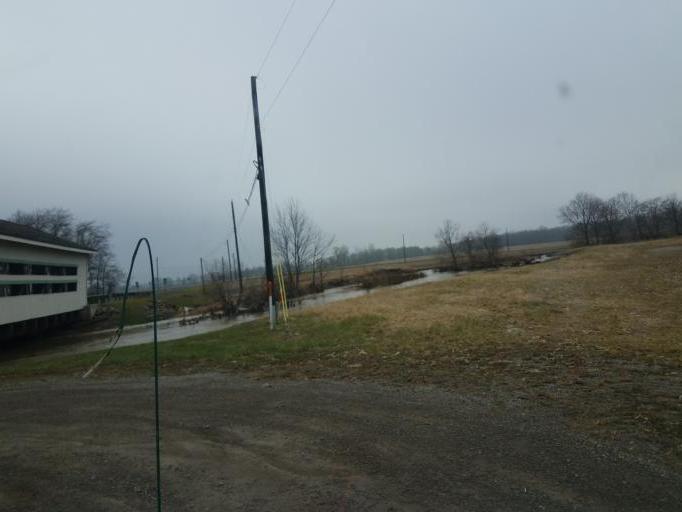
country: US
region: Ohio
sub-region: Champaign County
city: North Lewisburg
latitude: 40.2496
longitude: -83.5331
